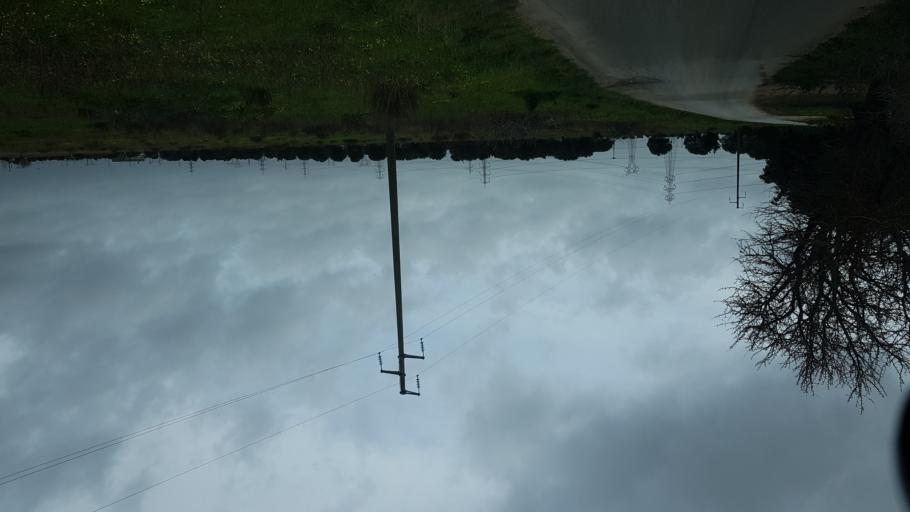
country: IT
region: Apulia
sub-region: Provincia di Brindisi
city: La Rosa
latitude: 40.6029
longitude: 17.9234
